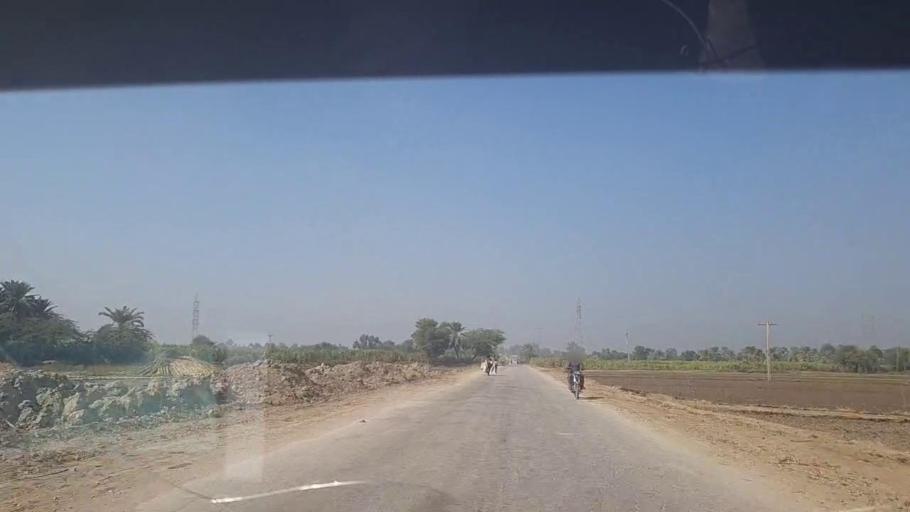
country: PK
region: Sindh
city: Kot Diji
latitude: 27.4257
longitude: 68.6566
